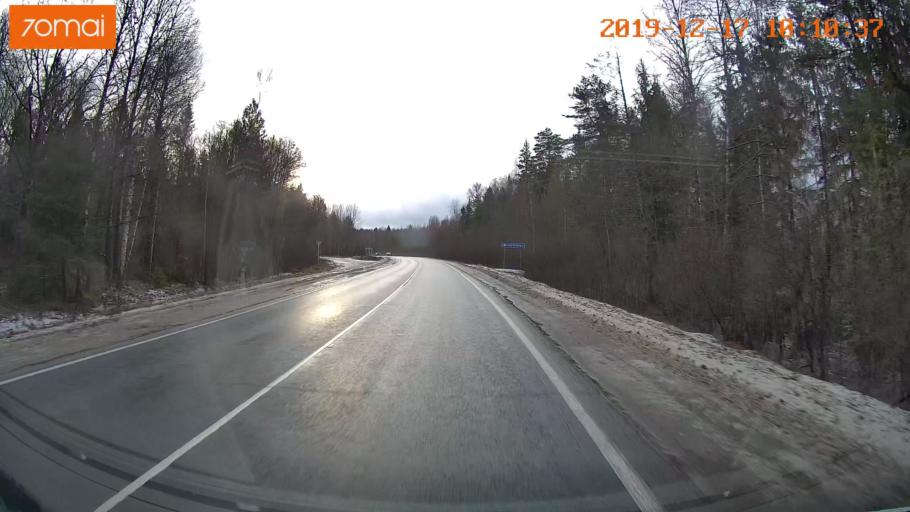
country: RU
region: Vladimir
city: Anopino
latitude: 55.8346
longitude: 40.6438
